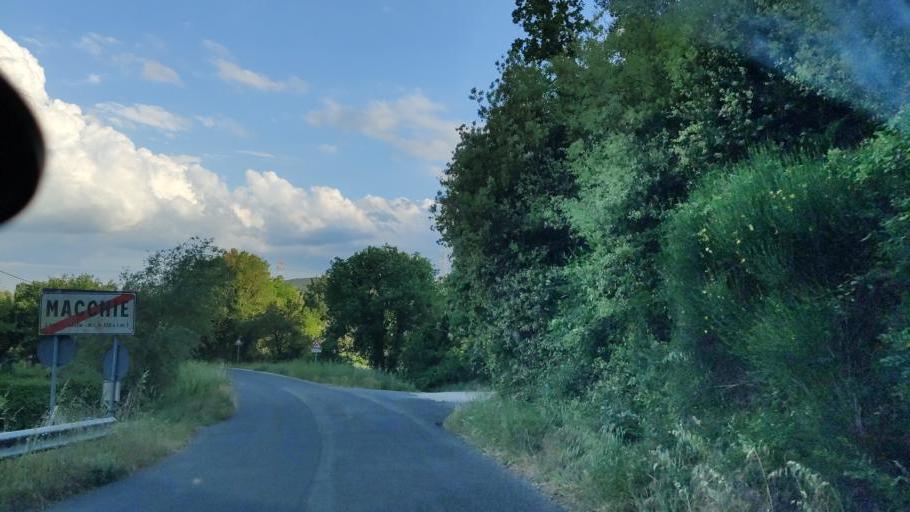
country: IT
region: Umbria
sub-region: Provincia di Terni
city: Lugnano in Teverina
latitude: 42.5953
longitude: 12.3726
